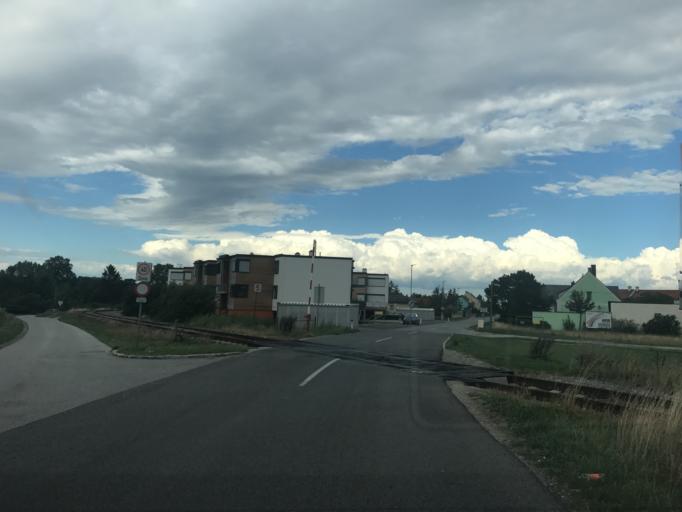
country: AT
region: Lower Austria
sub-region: Politischer Bezirk Wiener Neustadt
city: Theresienfeld
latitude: 47.8653
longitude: 16.1974
